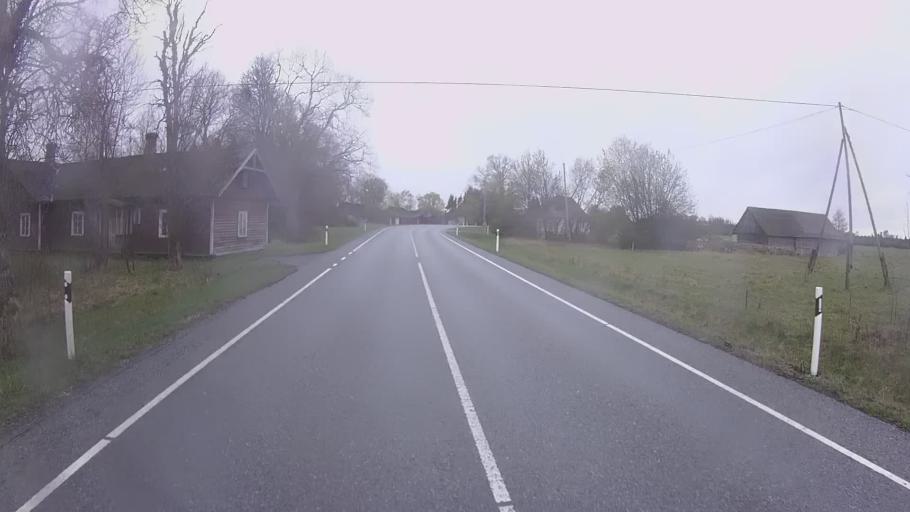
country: EE
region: Hiiumaa
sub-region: Kaerdla linn
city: Kardla
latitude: 58.9960
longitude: 22.5283
